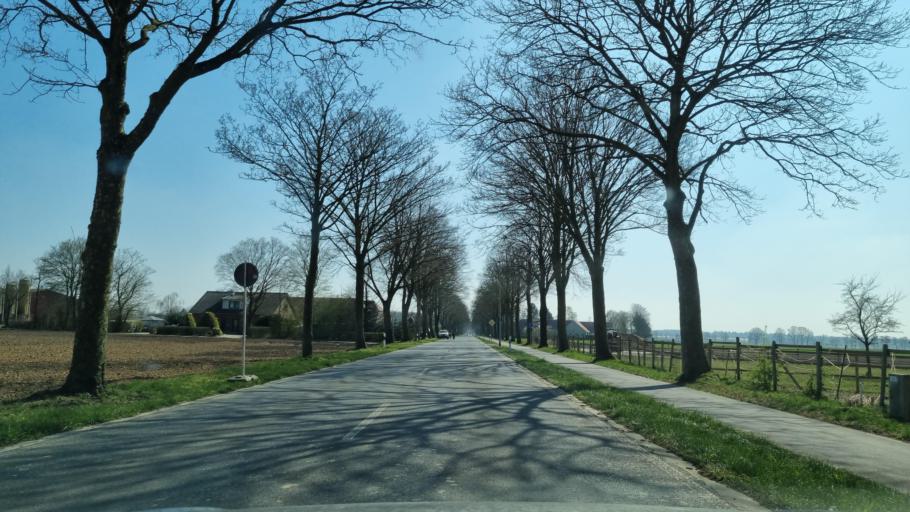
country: DE
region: North Rhine-Westphalia
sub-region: Regierungsbezirk Dusseldorf
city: Kleve
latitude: 51.7324
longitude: 6.1278
